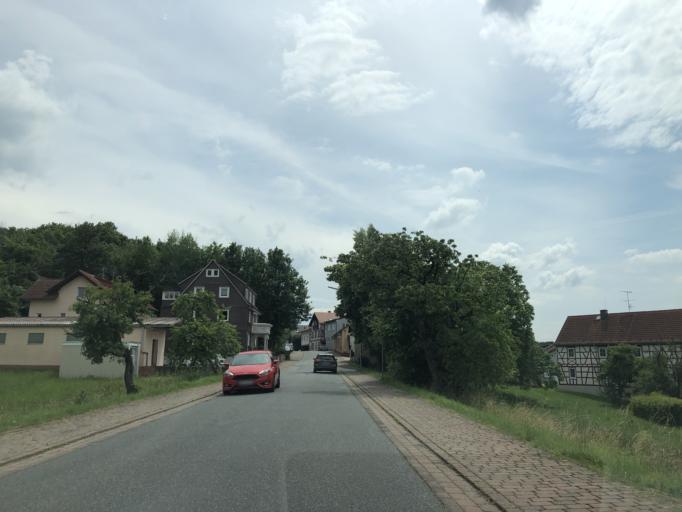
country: DE
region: Hesse
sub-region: Regierungsbezirk Darmstadt
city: Brensbach
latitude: 49.7410
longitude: 8.9199
